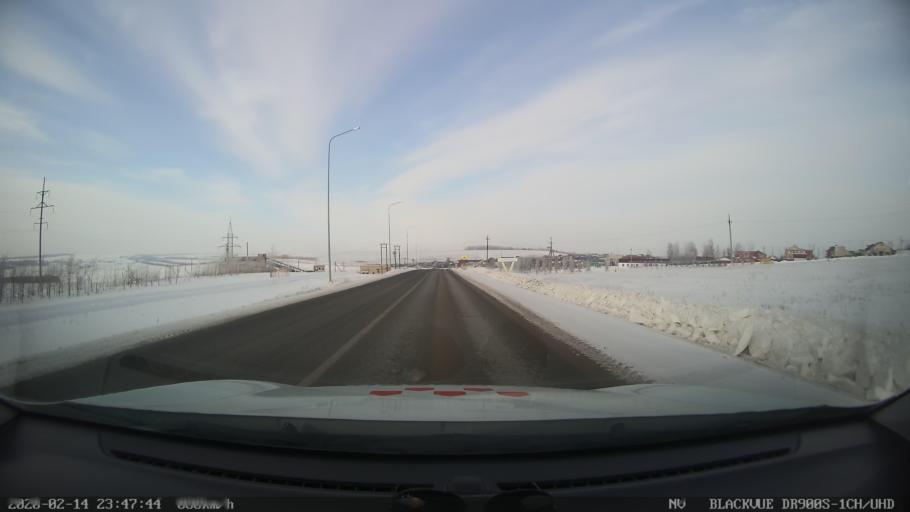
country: RU
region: Tatarstan
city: Kuybyshevskiy Zaton
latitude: 55.2421
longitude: 49.2072
